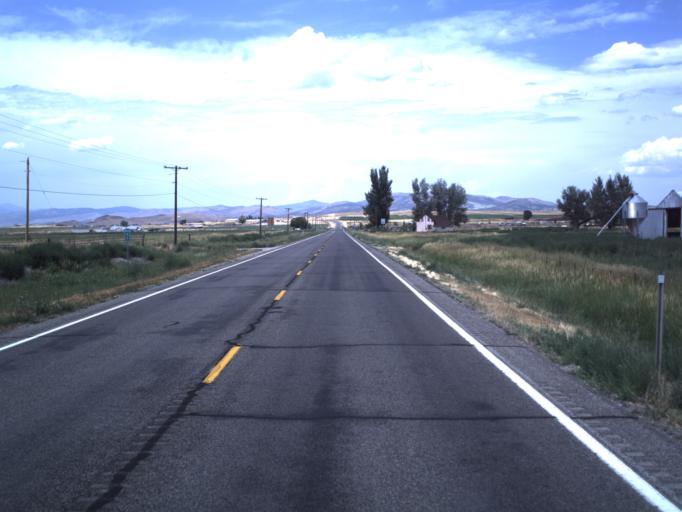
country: US
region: Utah
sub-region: Sanpete County
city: Moroni
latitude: 39.4802
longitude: -111.5629
